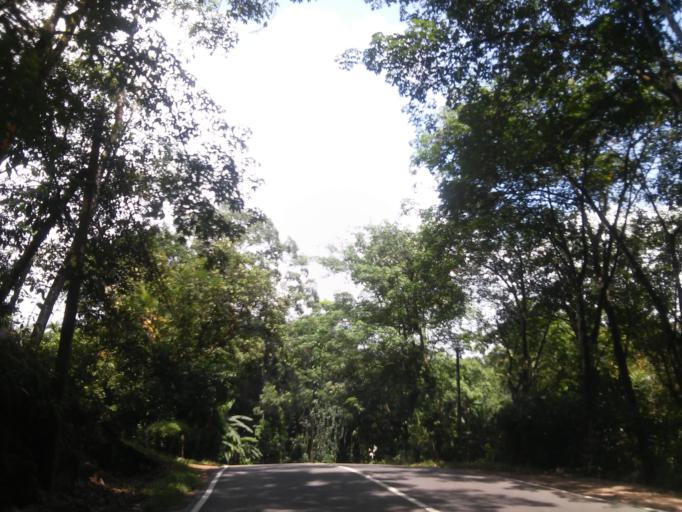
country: LK
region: Sabaragamuwa
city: Ratnapura
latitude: 6.7265
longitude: 80.3246
